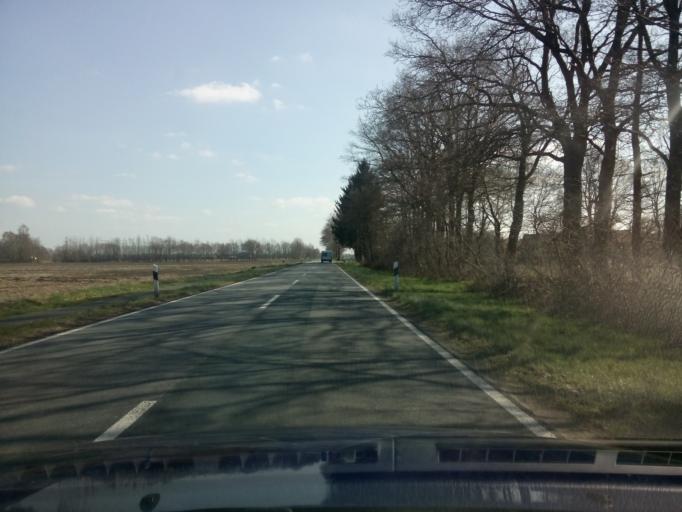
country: DE
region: Lower Saxony
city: Emlichheim
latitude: 52.5813
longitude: 6.8838
